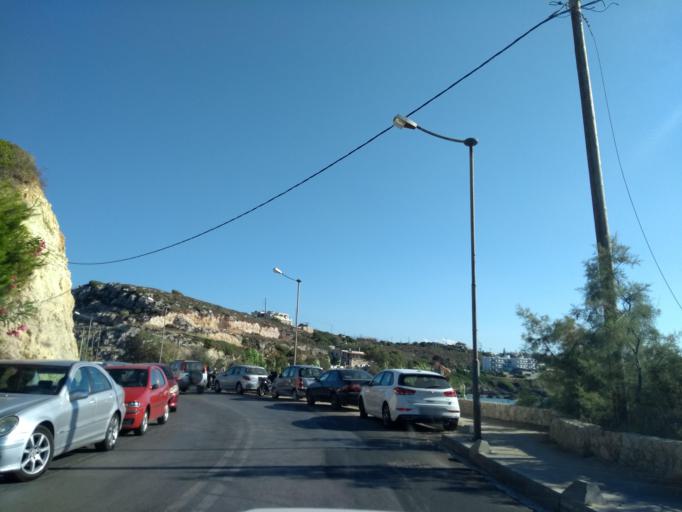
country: GR
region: Crete
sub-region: Nomos Chanias
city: Pithari
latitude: 35.5553
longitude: 24.0875
